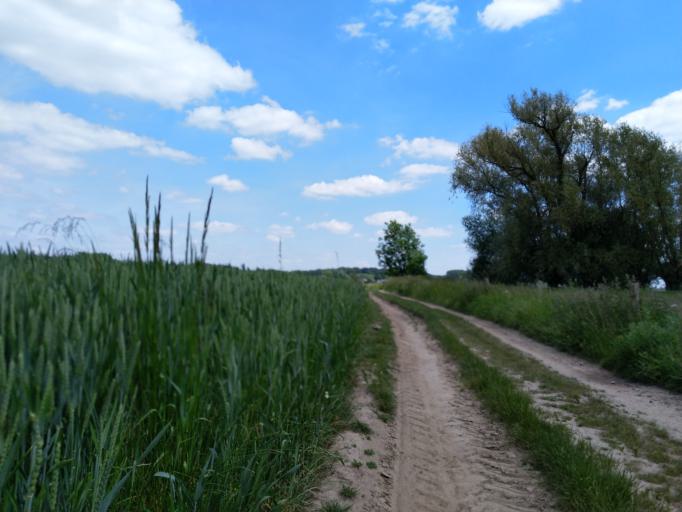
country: BE
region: Wallonia
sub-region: Province du Hainaut
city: Jurbise
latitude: 50.5233
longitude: 3.9510
